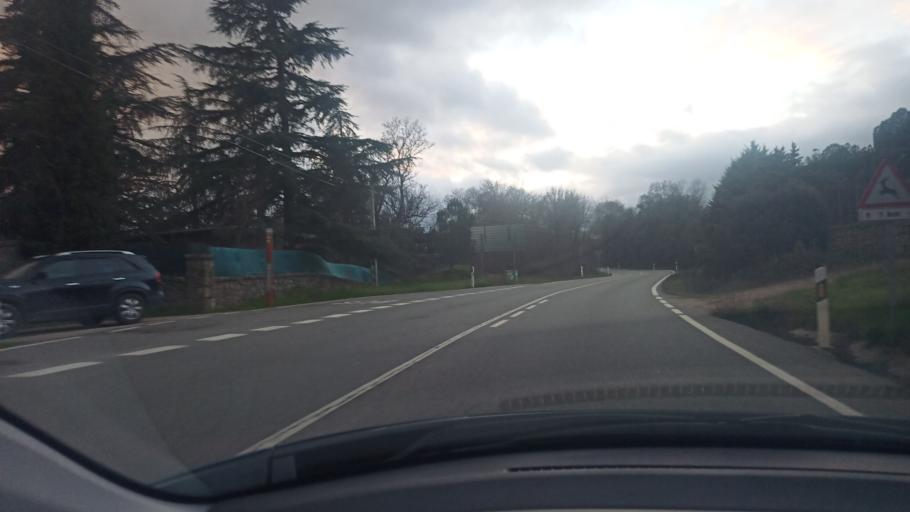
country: ES
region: Madrid
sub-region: Provincia de Madrid
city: El Escorial
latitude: 40.5439
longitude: -4.1129
